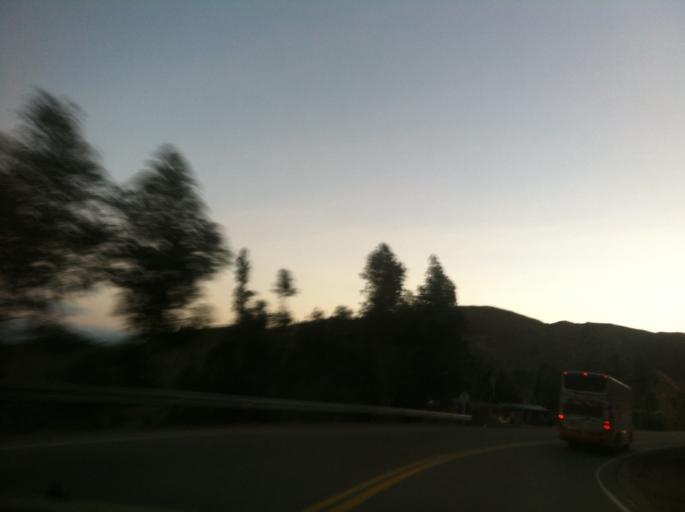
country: BO
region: Cochabamba
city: Irpa Irpa
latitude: -17.6657
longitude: -66.4110
